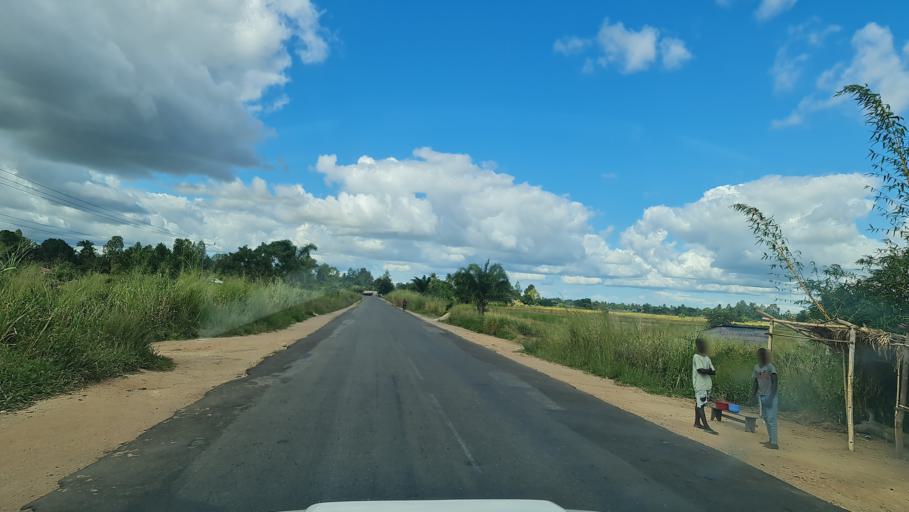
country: MZ
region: Zambezia
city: Quelimane
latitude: -17.6002
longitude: 36.7994
